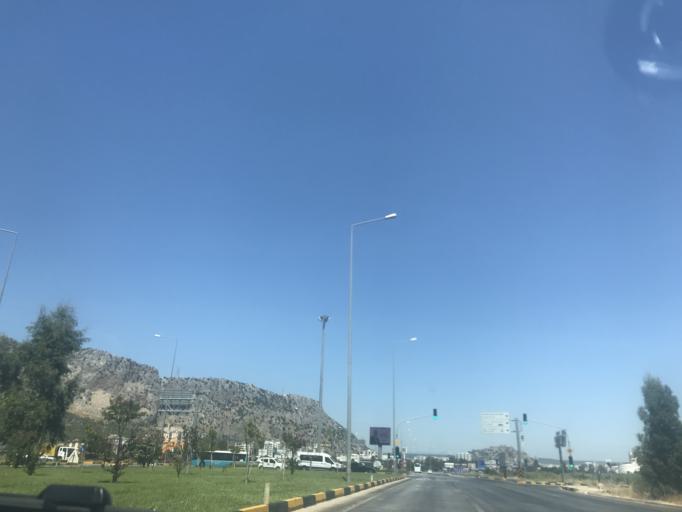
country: TR
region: Antalya
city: Cakirlar
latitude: 36.8351
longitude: 30.5956
